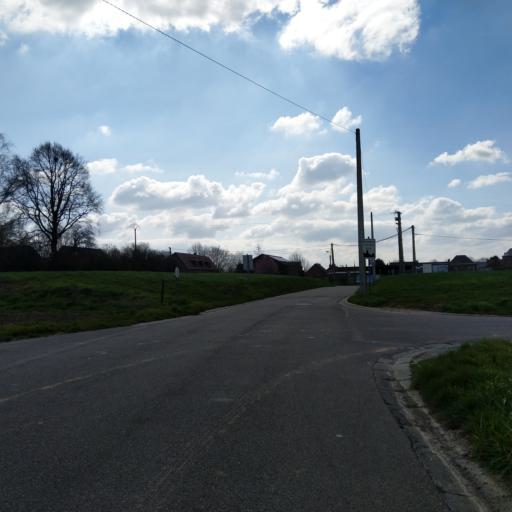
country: BE
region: Wallonia
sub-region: Province du Hainaut
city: Lens
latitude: 50.5666
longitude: 3.9431
